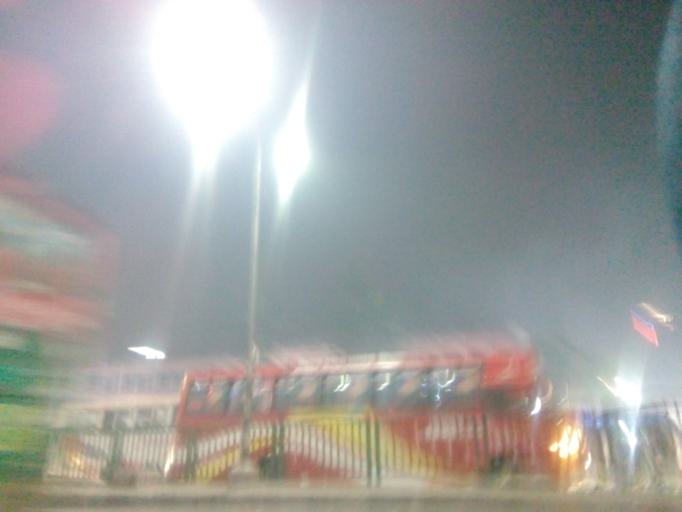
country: BD
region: Dhaka
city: Paltan
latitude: 23.7275
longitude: 90.4116
